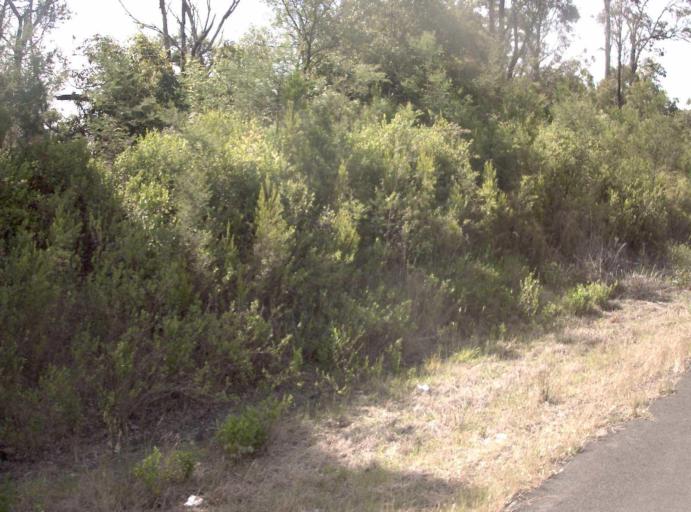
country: AU
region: Victoria
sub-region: East Gippsland
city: Lakes Entrance
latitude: -37.8466
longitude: 148.0413
